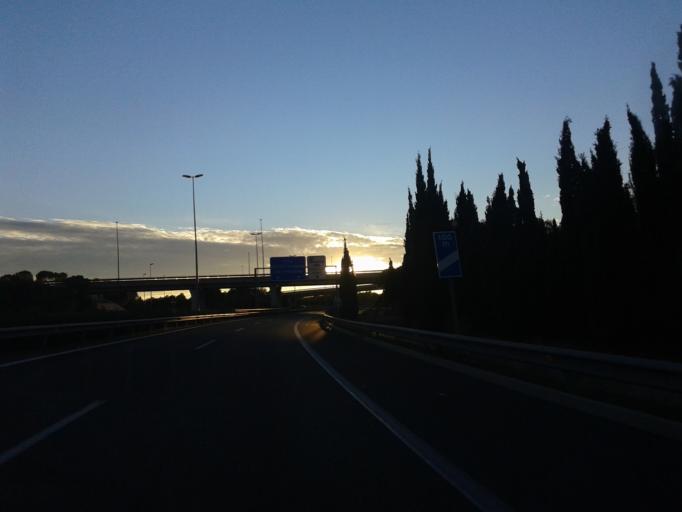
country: ES
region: Catalonia
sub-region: Provincia de Barcelona
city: Cubelles
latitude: 41.2099
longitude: 1.6598
